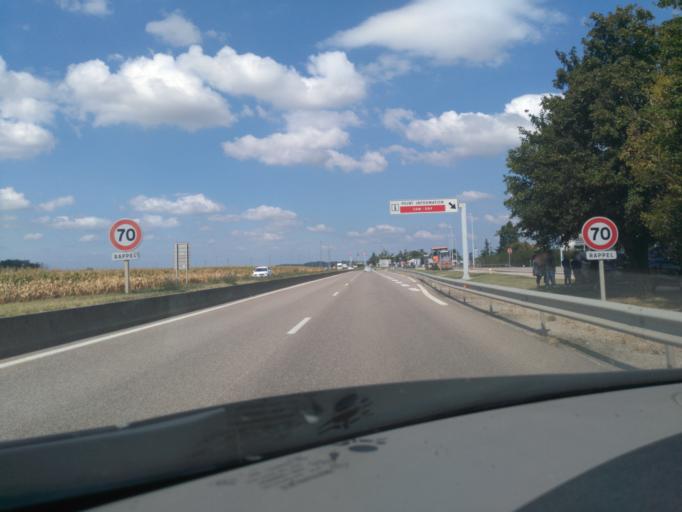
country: FR
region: Rhone-Alpes
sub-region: Departement du Rhone
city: Saint-Laurent-de-Mure
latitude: 45.7135
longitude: 5.0708
